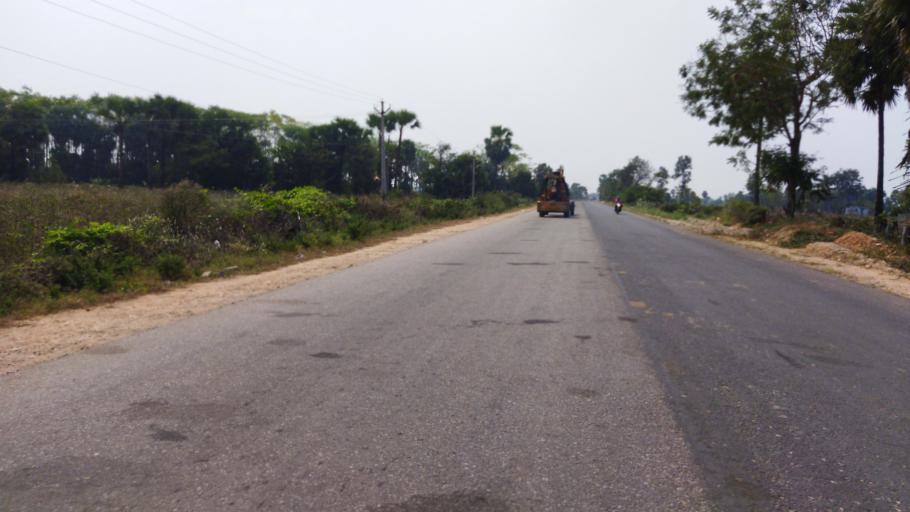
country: IN
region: Telangana
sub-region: Nalgonda
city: Nalgonda
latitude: 17.0996
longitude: 79.3404
